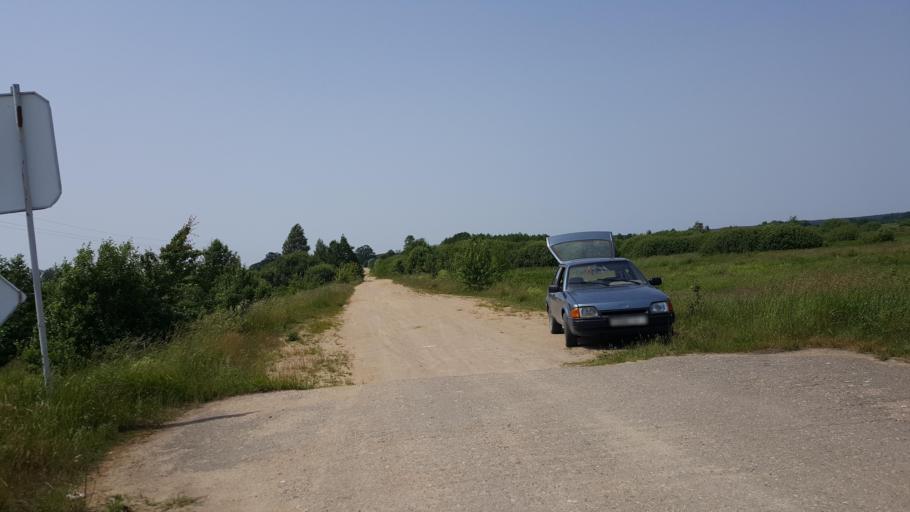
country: BY
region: Brest
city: Kamyanyets
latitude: 52.4757
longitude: 23.8993
